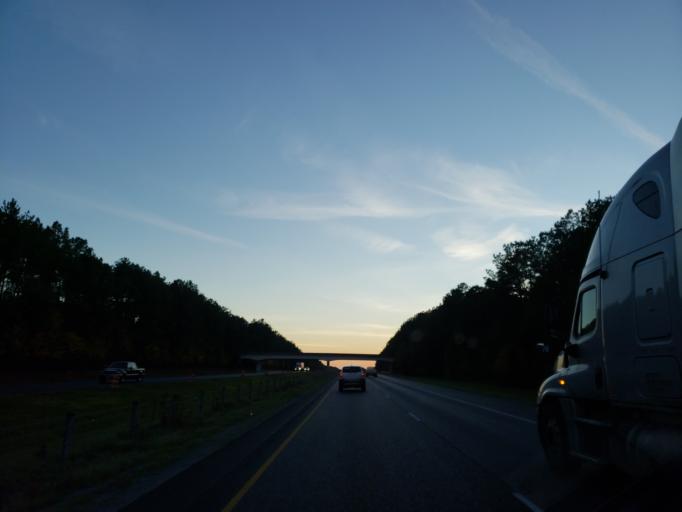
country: US
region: Alabama
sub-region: Sumter County
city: York
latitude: 32.5564
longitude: -88.2643
